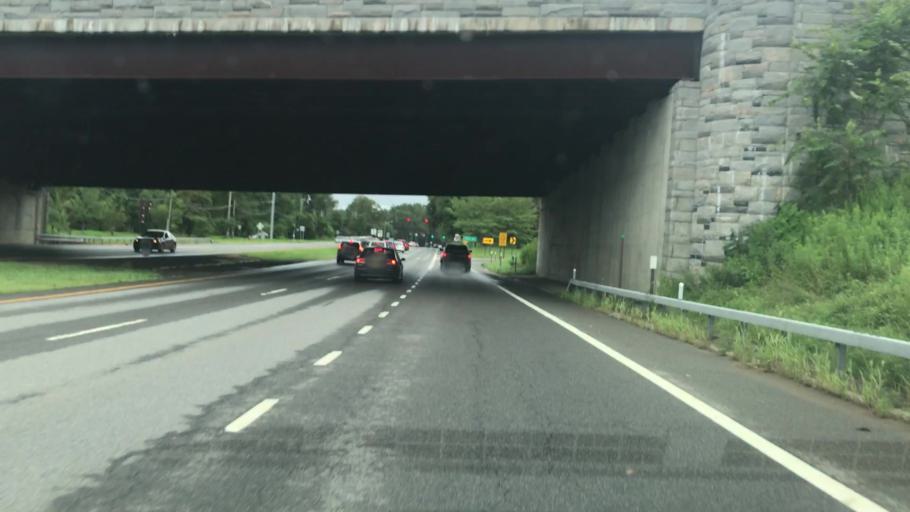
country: US
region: New York
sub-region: Westchester County
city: Shrub Oak
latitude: 41.3326
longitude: -73.8171
